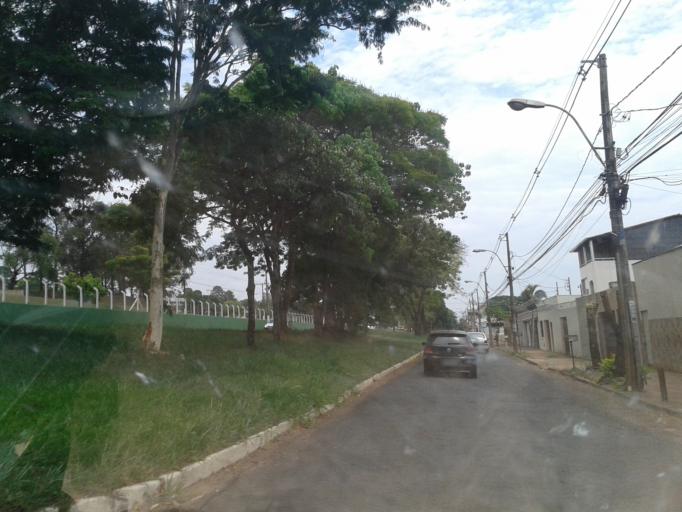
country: BR
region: Minas Gerais
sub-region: Uberlandia
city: Uberlandia
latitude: -18.9246
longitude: -48.3050
